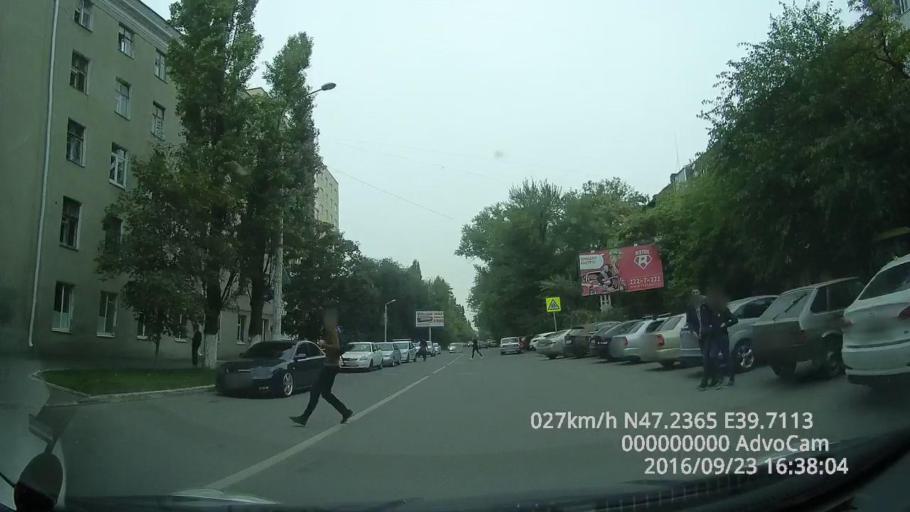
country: RU
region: Rostov
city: Rostov-na-Donu
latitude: 47.2365
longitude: 39.7110
